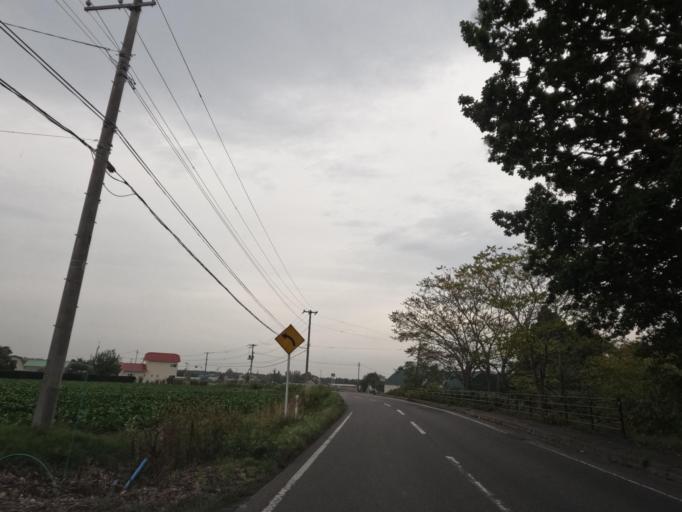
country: JP
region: Hokkaido
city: Date
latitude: 42.5023
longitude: 140.8750
